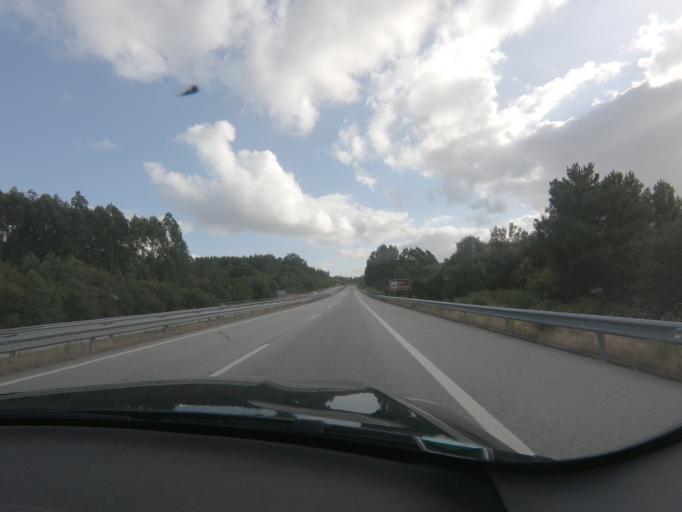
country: PT
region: Viseu
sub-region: Viseu
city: Campo
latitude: 40.7205
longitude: -7.9248
